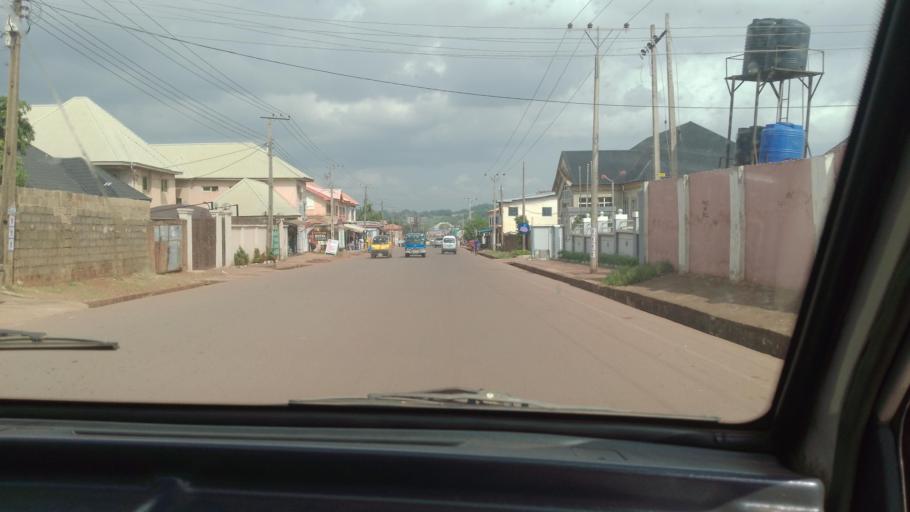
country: NG
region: Enugu
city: Enugu
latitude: 6.4797
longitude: 7.5026
